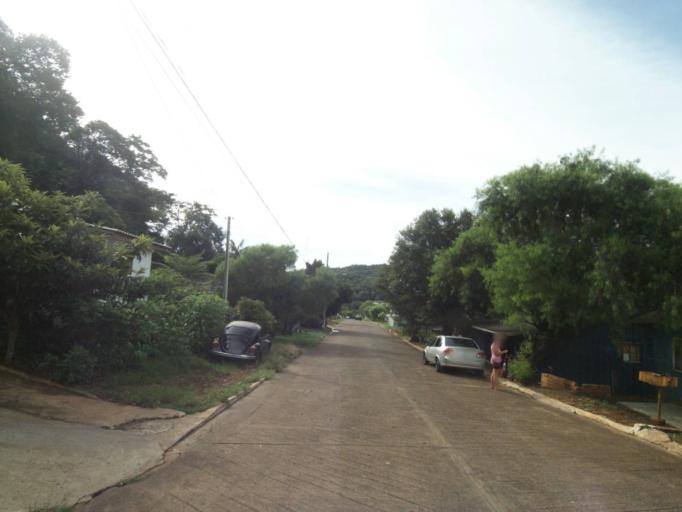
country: BR
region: Parana
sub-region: Guaraniacu
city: Guaraniacu
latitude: -25.1016
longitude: -52.8735
